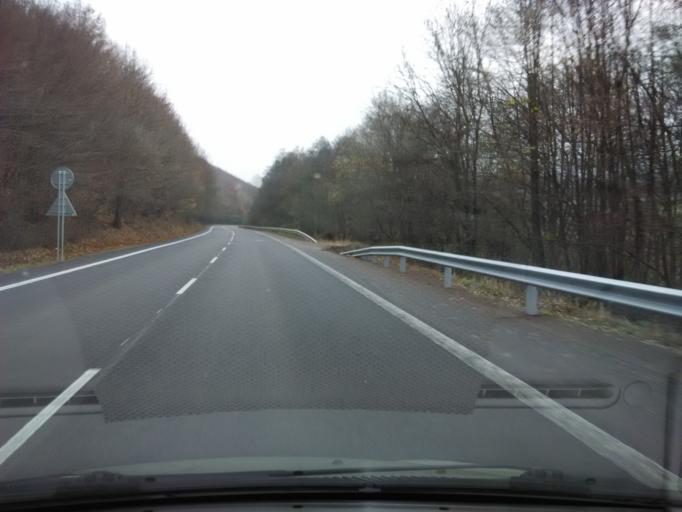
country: SK
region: Banskobystricky
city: Ziar nad Hronom
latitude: 48.6242
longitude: 18.8975
